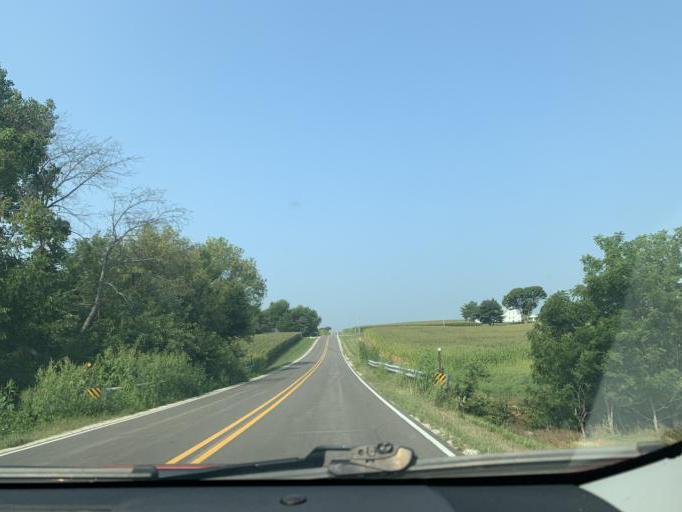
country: US
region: Illinois
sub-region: Whiteside County
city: Sterling
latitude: 41.8441
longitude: -89.7633
